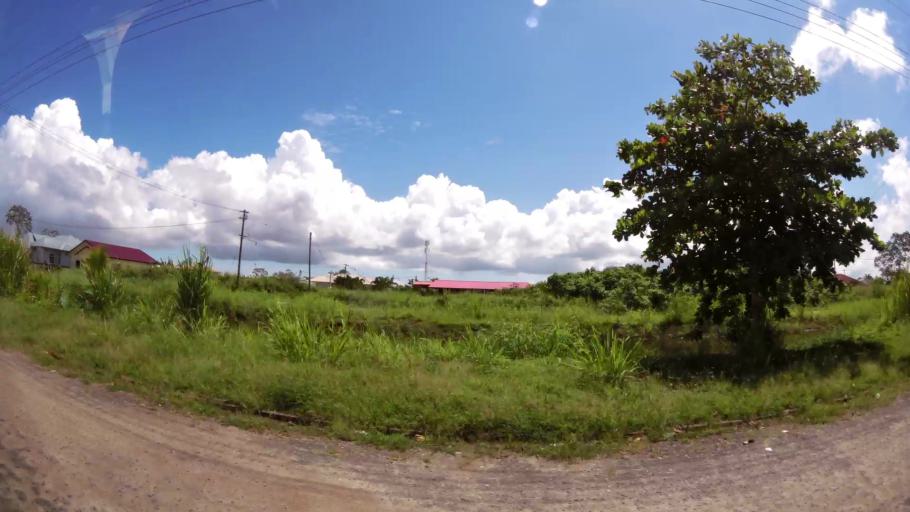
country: SR
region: Paramaribo
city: Paramaribo
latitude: 5.8653
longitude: -55.1400
